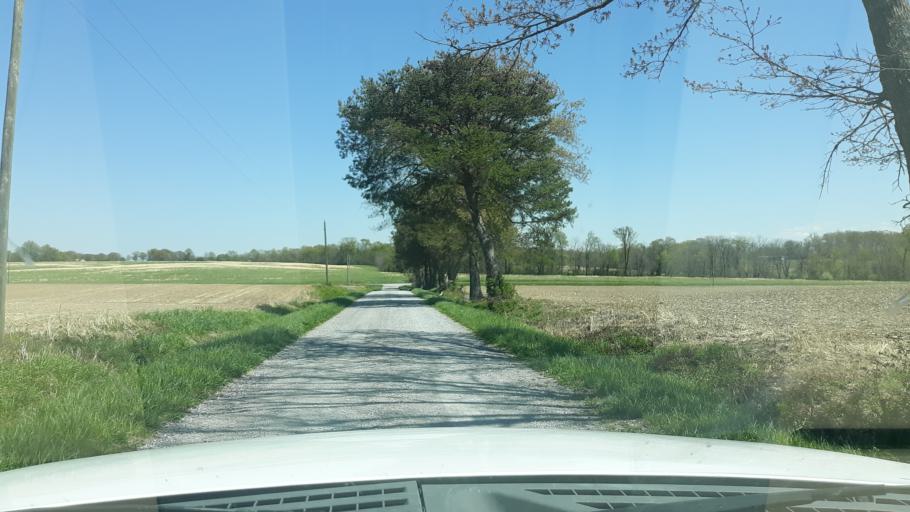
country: US
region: Illinois
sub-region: Saline County
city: Harrisburg
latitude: 37.8887
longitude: -88.6725
